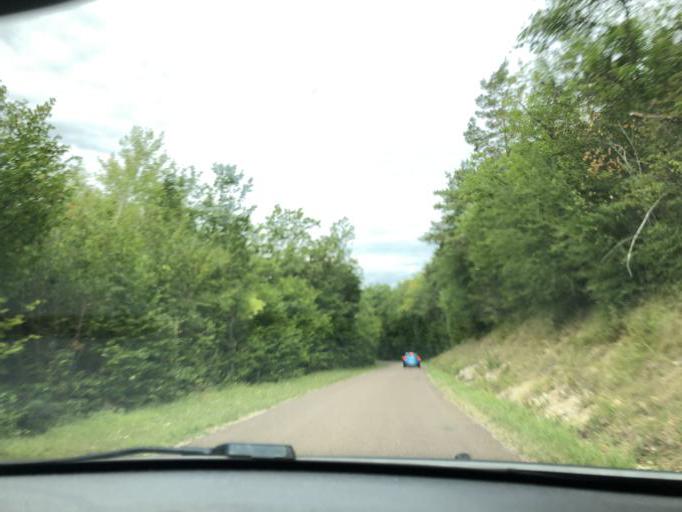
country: FR
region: Bourgogne
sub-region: Departement de l'Yonne
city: Chablis
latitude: 47.7784
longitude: 3.8230
